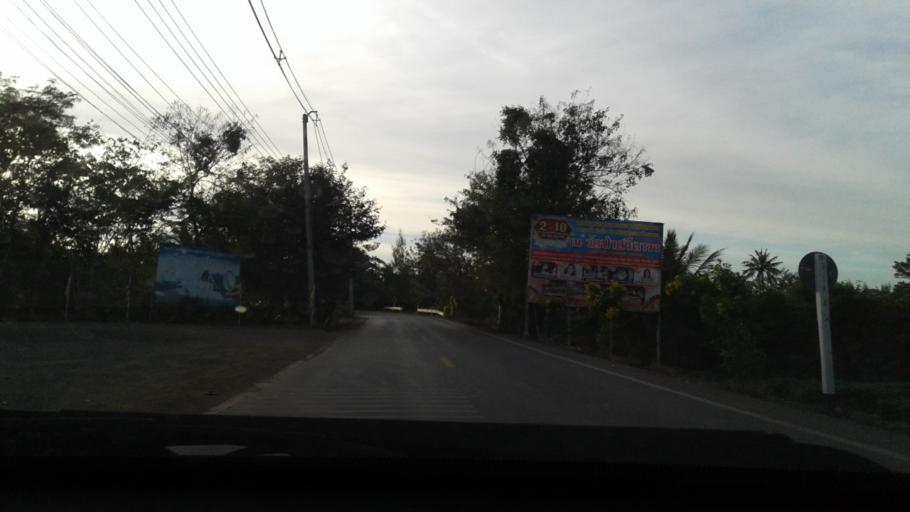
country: TH
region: Nonthaburi
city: Sai Noi
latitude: 13.9036
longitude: 100.2515
